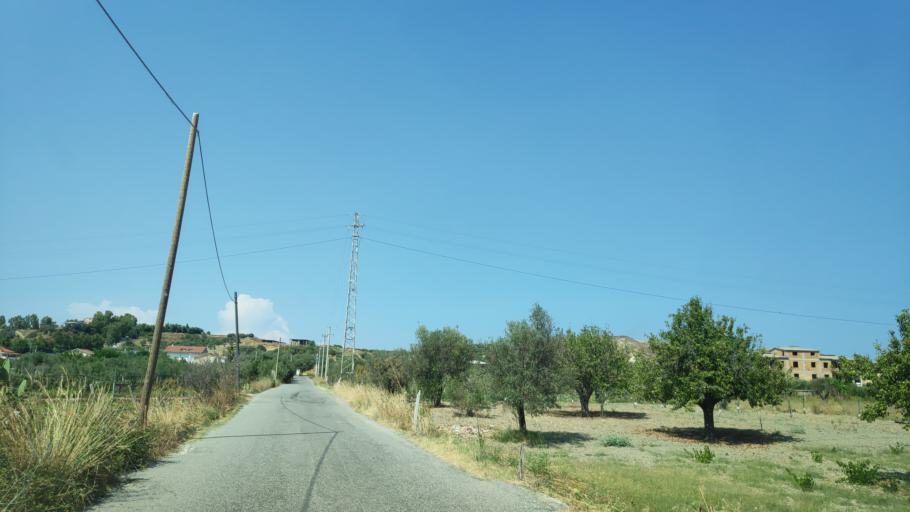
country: IT
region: Calabria
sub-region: Provincia di Reggio Calabria
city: Monasterace Marina
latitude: 38.4249
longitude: 16.5436
